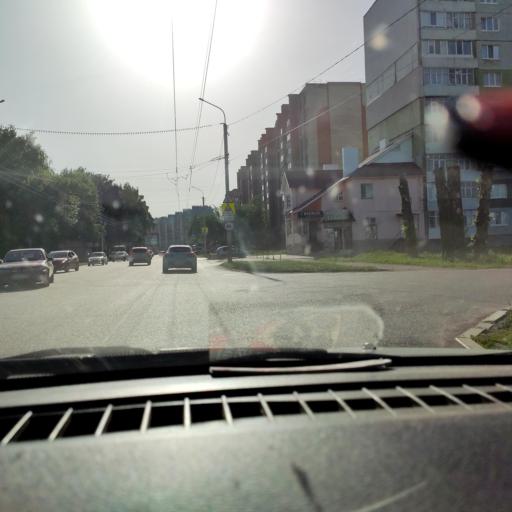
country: RU
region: Bashkortostan
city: Sterlitamak
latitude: 53.6377
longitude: 55.9051
